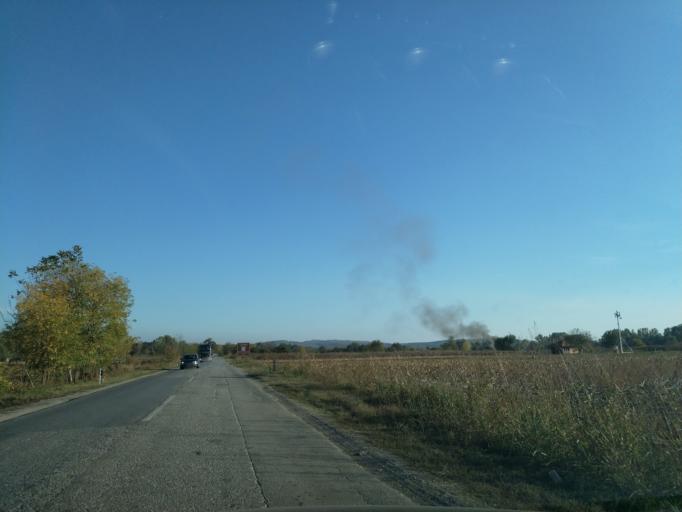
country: RS
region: Central Serbia
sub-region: Pomoravski Okrug
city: Svilajnac
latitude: 44.2337
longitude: 21.1395
